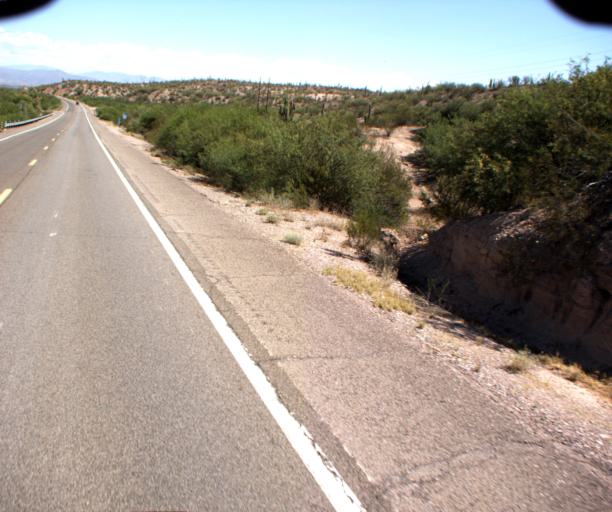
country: US
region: Arizona
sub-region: Pinal County
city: Mammoth
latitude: 32.8728
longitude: -110.7112
